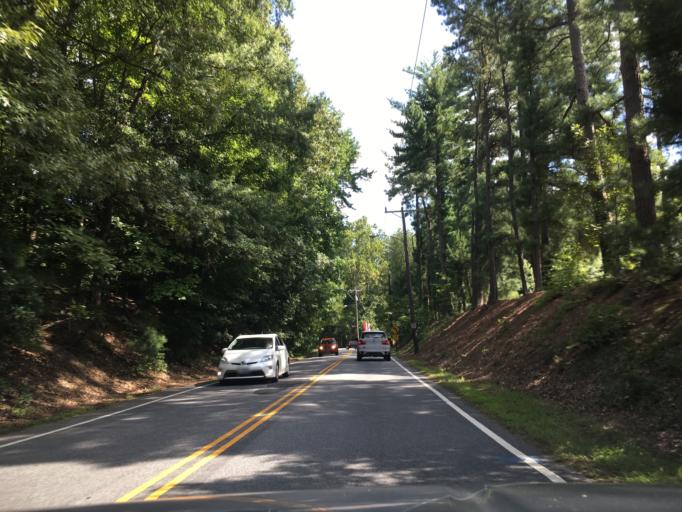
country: US
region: Virginia
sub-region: Henrico County
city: Tuckahoe
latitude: 37.5806
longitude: -77.5351
